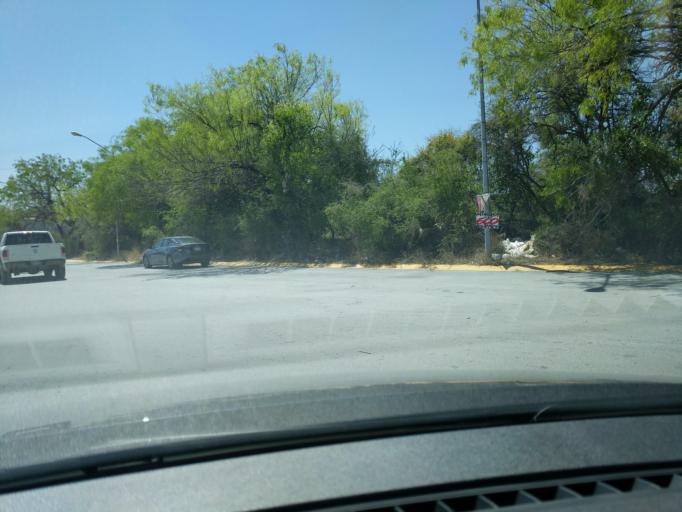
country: MX
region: Nuevo Leon
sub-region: Apodaca
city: Artemio Trevino
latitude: 25.8173
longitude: -100.1531
